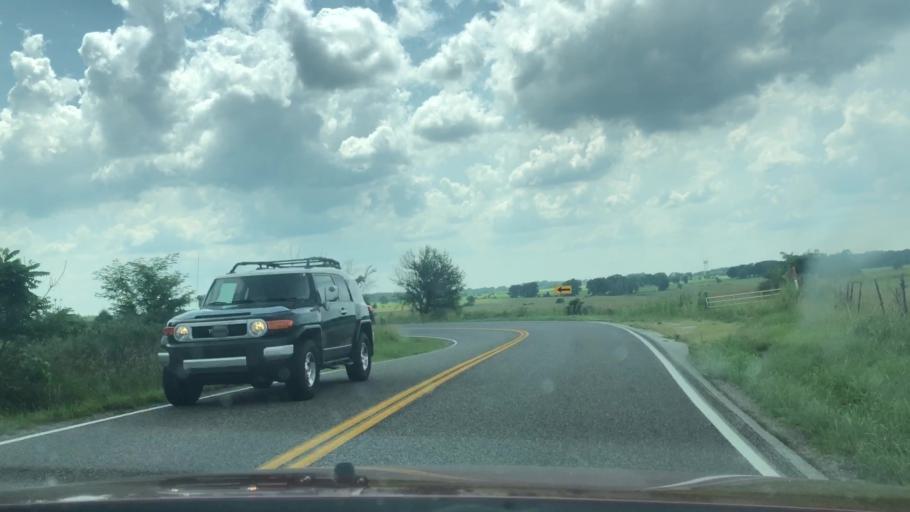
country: US
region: Missouri
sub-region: Christian County
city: Ozark
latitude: 36.9412
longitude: -93.2524
